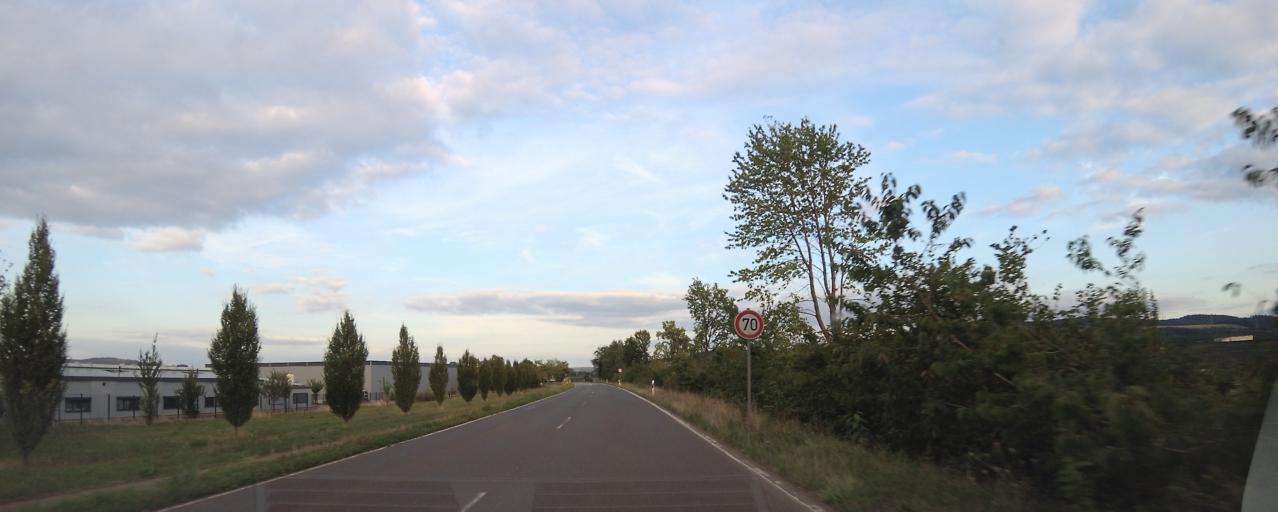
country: DE
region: Rheinland-Pfalz
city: Fohren
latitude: 49.8571
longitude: 6.7800
